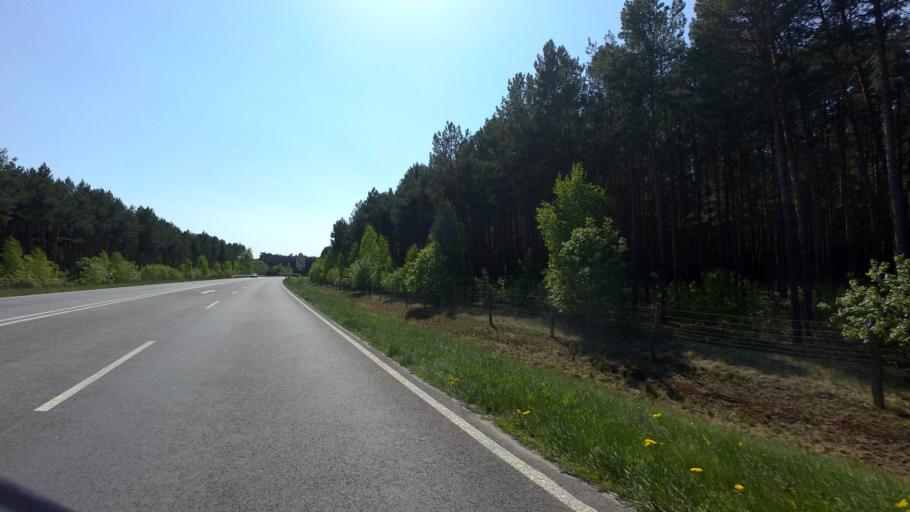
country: DE
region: Brandenburg
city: Beeskow
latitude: 52.1524
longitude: 14.2155
